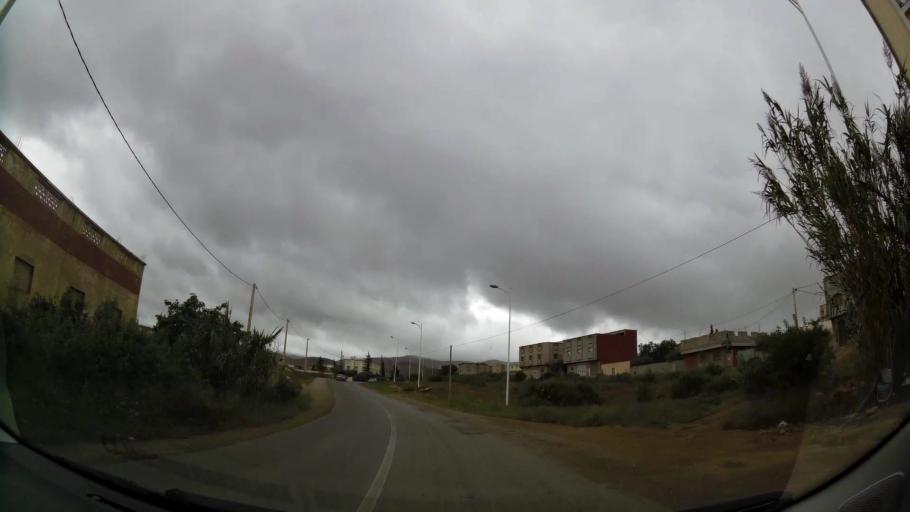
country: MA
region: Oriental
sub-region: Nador
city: Midar
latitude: 35.0577
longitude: -3.4651
